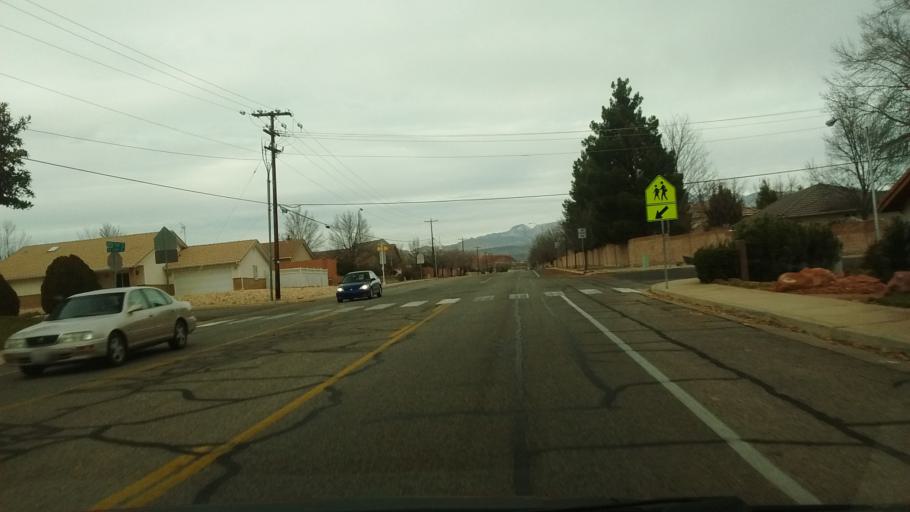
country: US
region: Utah
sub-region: Washington County
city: Washington
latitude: 37.1140
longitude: -113.5317
